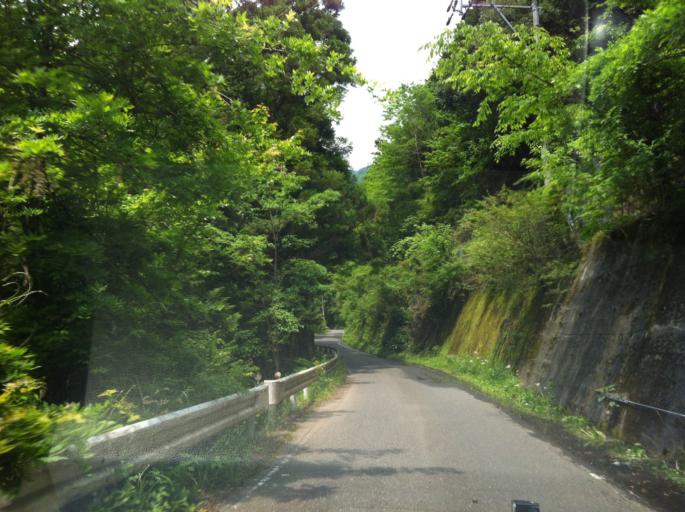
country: JP
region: Shizuoka
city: Shizuoka-shi
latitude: 35.1691
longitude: 138.3139
